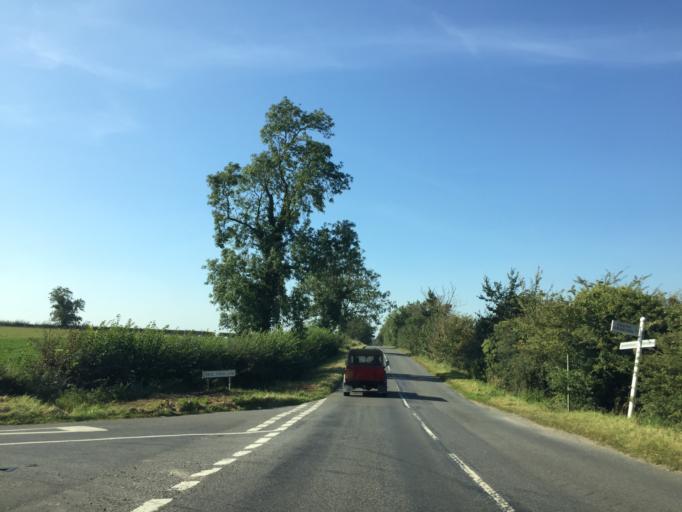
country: GB
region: England
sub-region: Leicestershire
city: Asfordby
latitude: 52.6933
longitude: -0.9825
